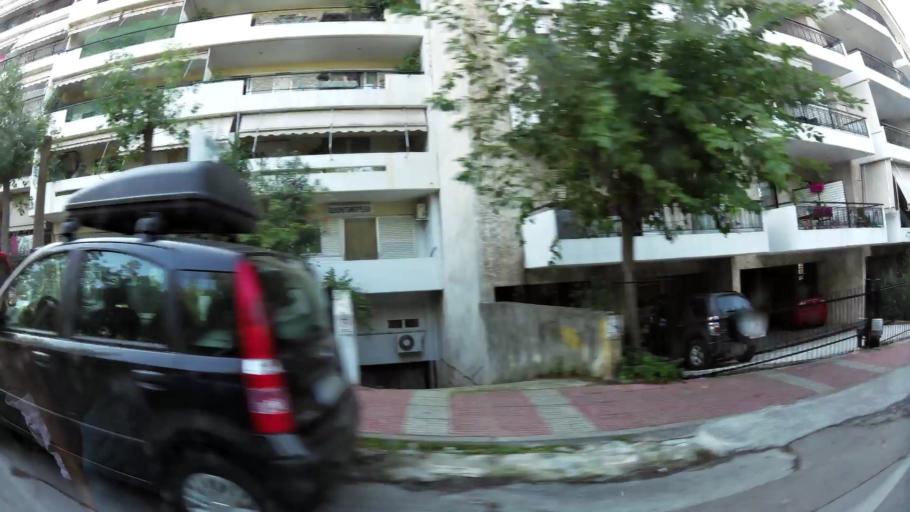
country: GR
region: Attica
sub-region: Nomarchia Athinas
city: Papagou
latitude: 37.9839
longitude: 23.7735
